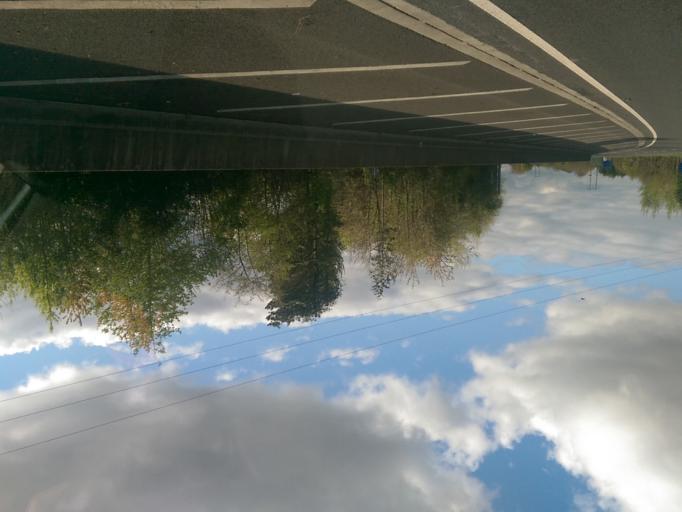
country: IE
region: Leinster
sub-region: An Iarmhi
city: Athlone
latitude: 53.4237
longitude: -7.8929
